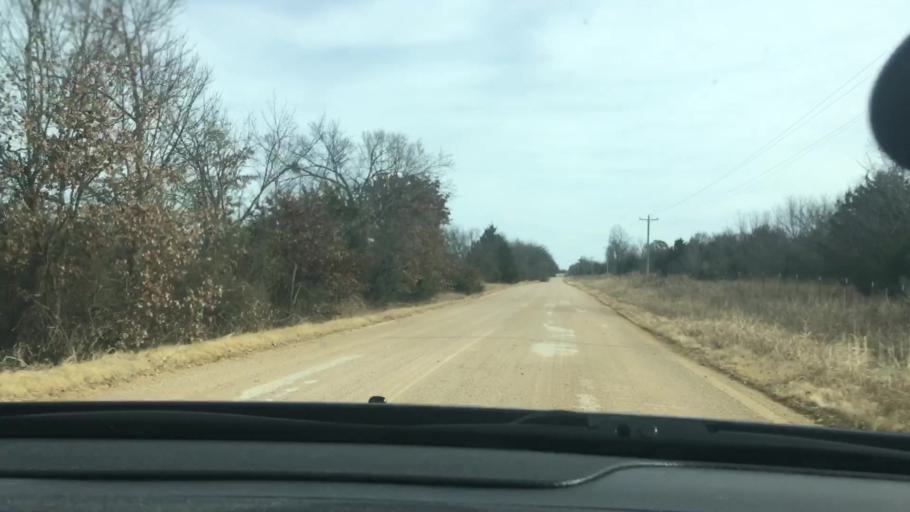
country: US
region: Oklahoma
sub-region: Murray County
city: Sulphur
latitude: 34.4064
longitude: -96.9450
